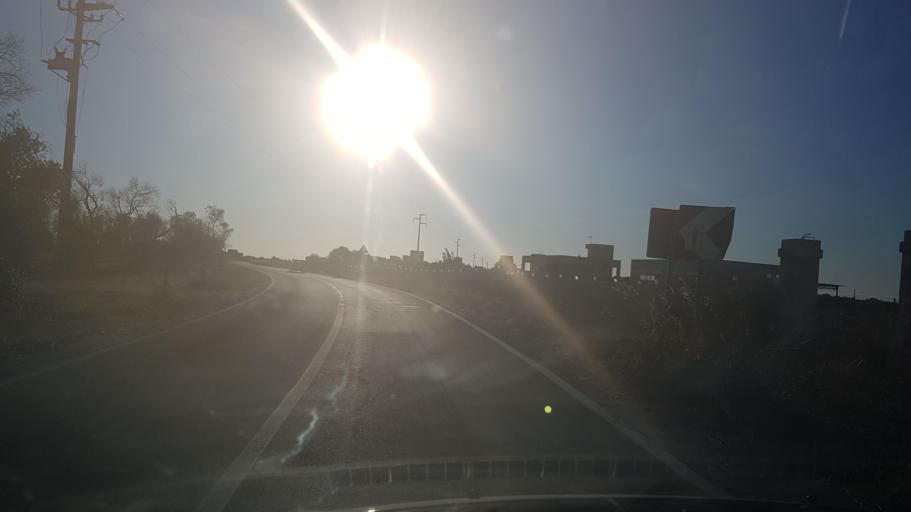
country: IT
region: Apulia
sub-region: Provincia di Lecce
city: Struda
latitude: 40.3292
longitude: 18.3056
